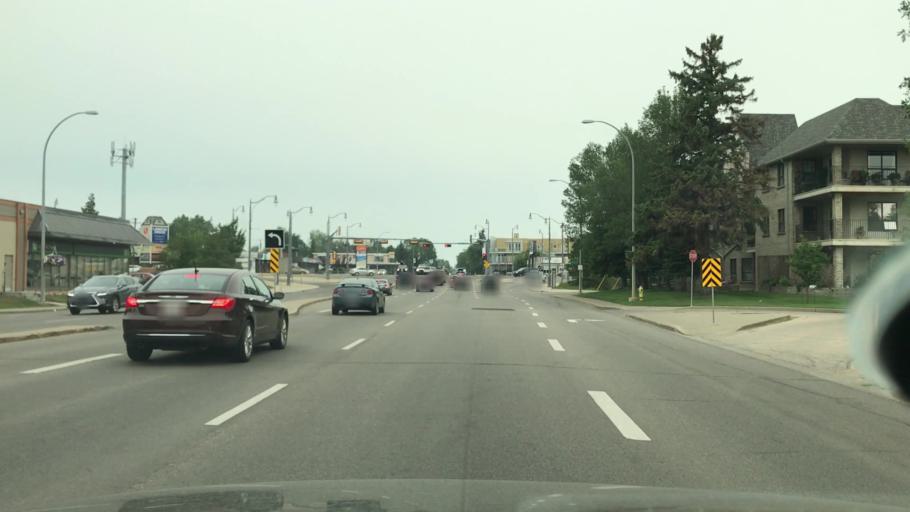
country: CA
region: Alberta
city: St. Albert
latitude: 53.5403
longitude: -113.5779
